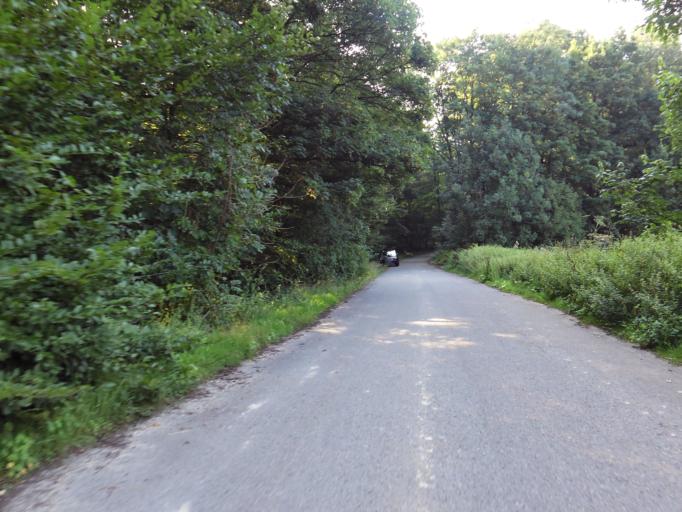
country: DE
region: North Rhine-Westphalia
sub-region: Regierungsbezirk Koln
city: Herzogenrath
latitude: 50.9073
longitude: 6.0871
